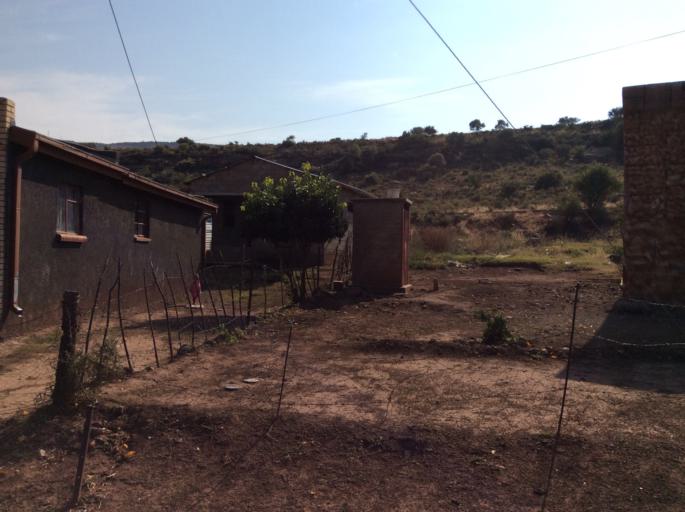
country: LS
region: Mafeteng
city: Mafeteng
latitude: -29.7178
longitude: 27.0350
